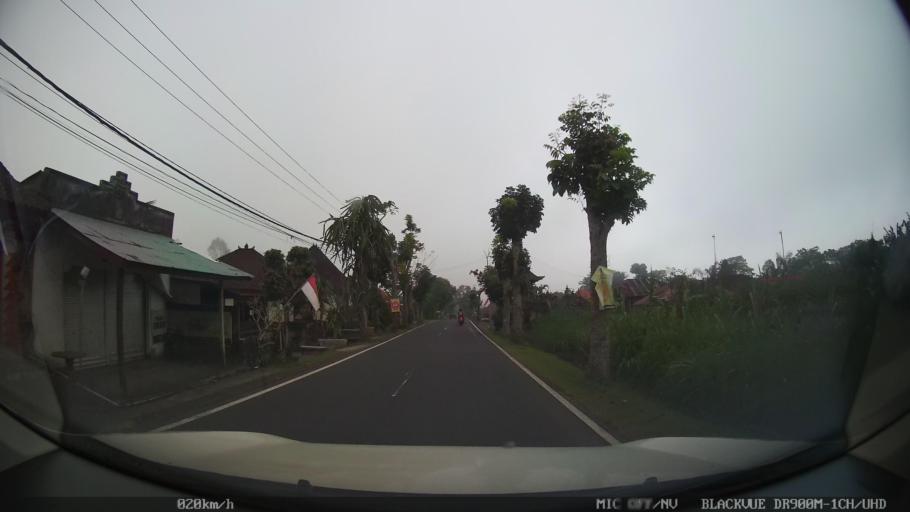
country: ID
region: Bali
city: Banjar Kedisan
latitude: -8.3034
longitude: 115.3078
